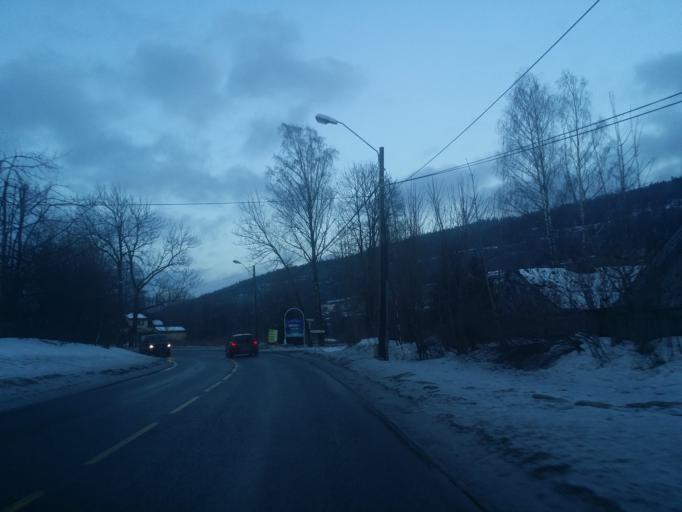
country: NO
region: Akershus
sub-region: Baerum
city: Skui
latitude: 59.9229
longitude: 10.4934
